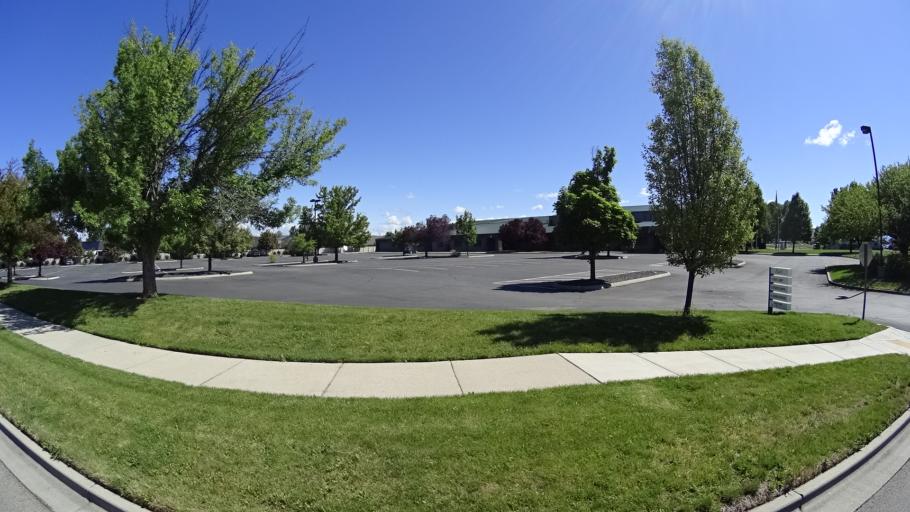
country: US
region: Idaho
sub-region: Ada County
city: Meridian
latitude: 43.6204
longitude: -116.3620
